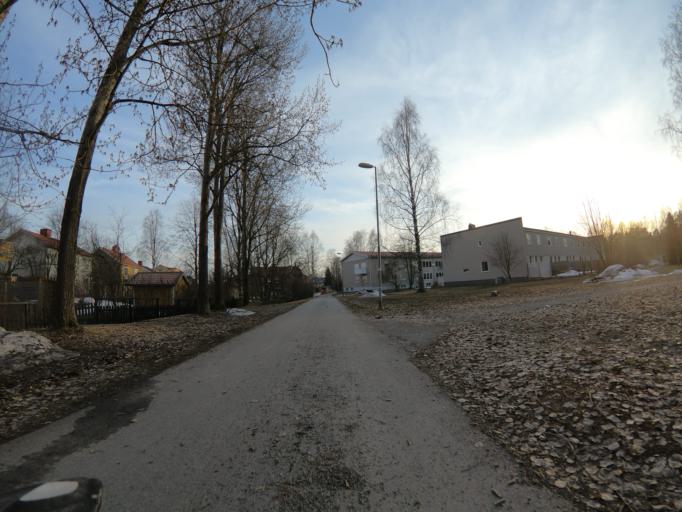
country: SE
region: Vaesterbotten
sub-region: Umea Kommun
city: Umea
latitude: 63.8389
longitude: 20.2774
